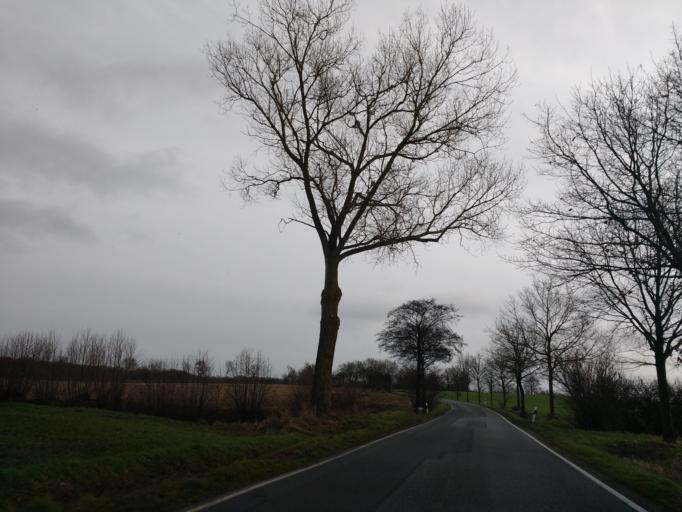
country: DE
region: Schleswig-Holstein
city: Susel
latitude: 54.0132
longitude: 10.6654
